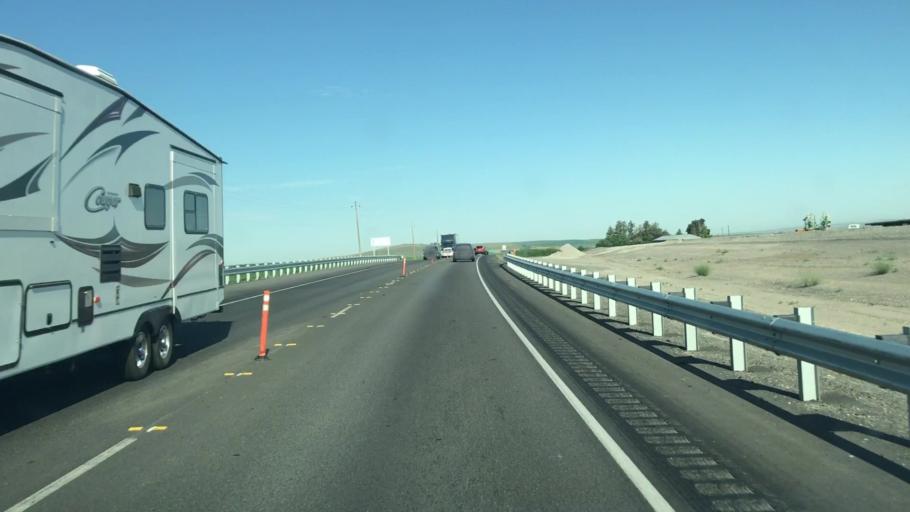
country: US
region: Idaho
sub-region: Twin Falls County
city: Hansen
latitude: 42.5745
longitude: -114.1490
